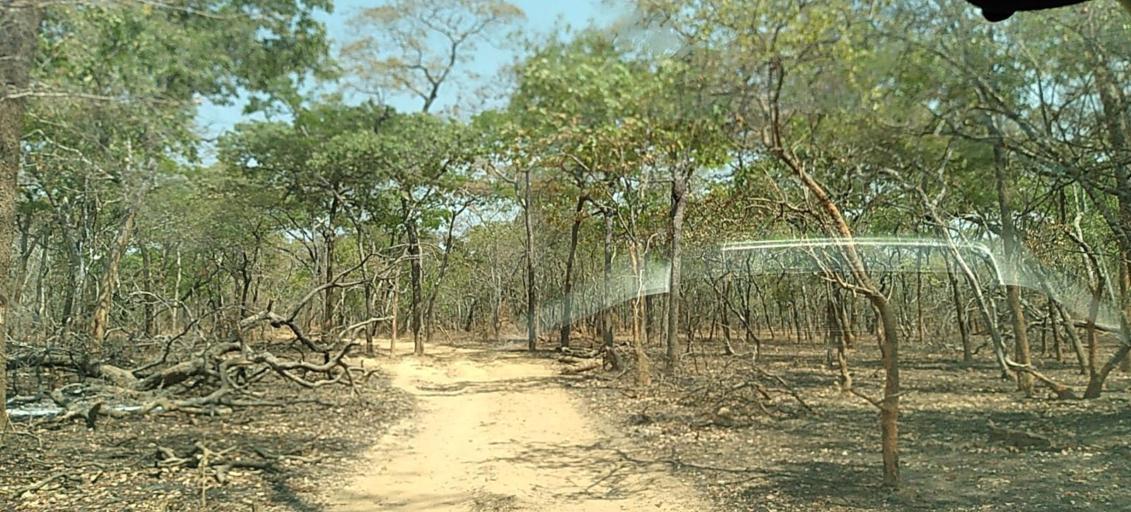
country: ZM
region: North-Western
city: Kasempa
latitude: -13.3923
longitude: 25.6203
